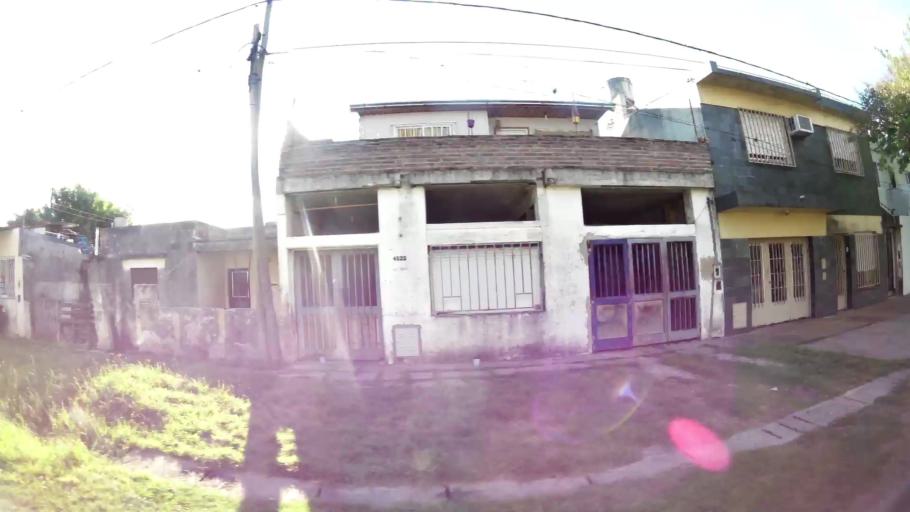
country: AR
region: Santa Fe
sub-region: Departamento de Rosario
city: Rosario
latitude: -32.9872
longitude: -60.6700
